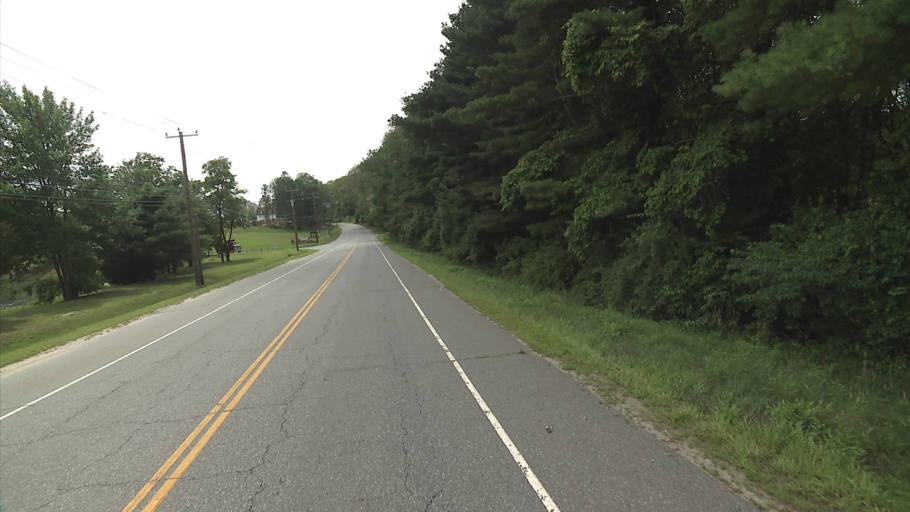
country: US
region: Connecticut
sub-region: Middlesex County
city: Deep River Center
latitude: 41.3663
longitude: -72.4643
